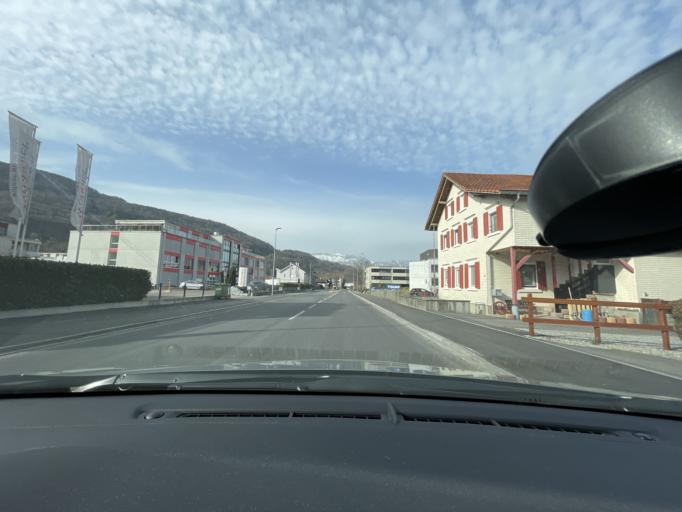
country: CH
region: Saint Gallen
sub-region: Wahlkreis Werdenberg
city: Sevelen
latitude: 47.1250
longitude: 9.4871
